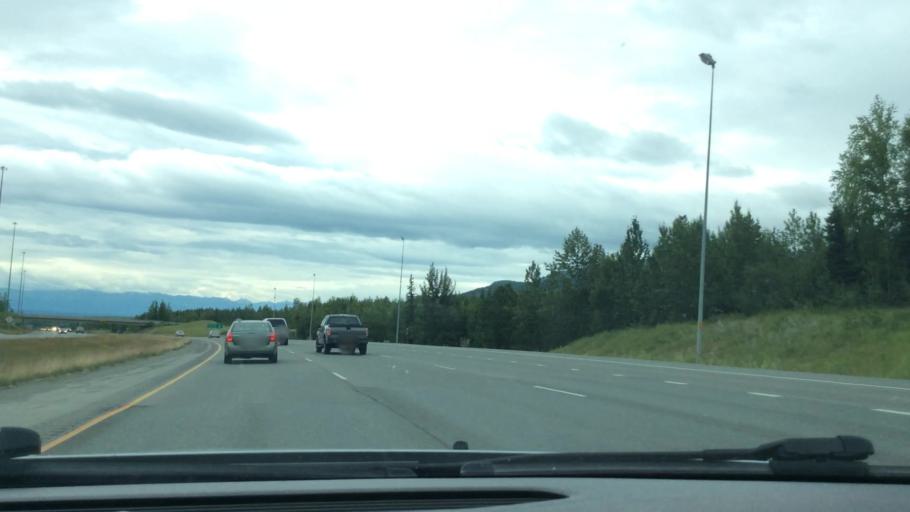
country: US
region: Alaska
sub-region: Anchorage Municipality
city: Eagle River
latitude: 61.2912
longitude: -149.5914
